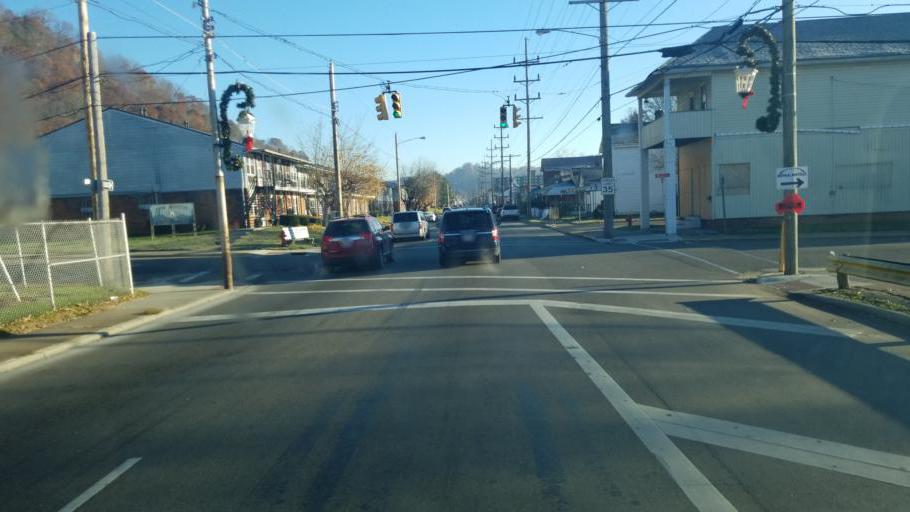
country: US
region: Ohio
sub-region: Scioto County
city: New Boston
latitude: 38.7482
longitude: -82.9426
